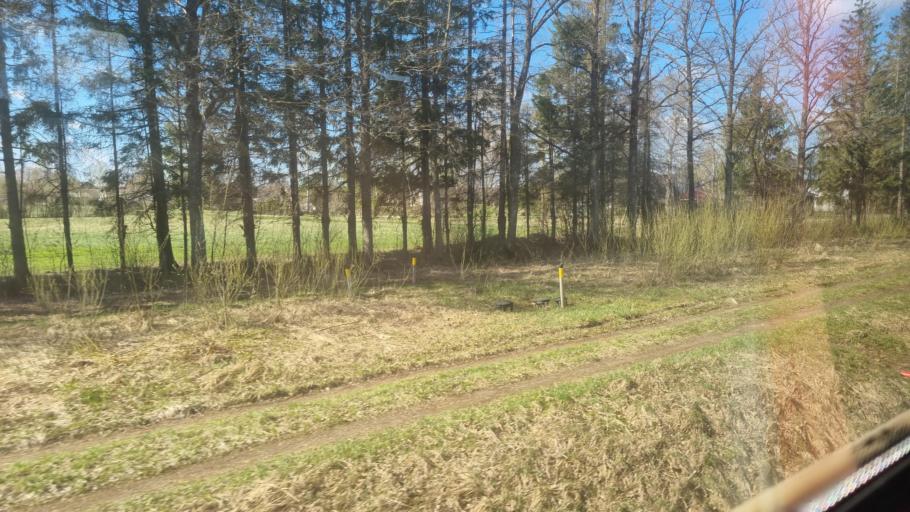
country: LV
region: Lielvarde
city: Lielvarde
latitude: 56.7204
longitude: 24.8210
